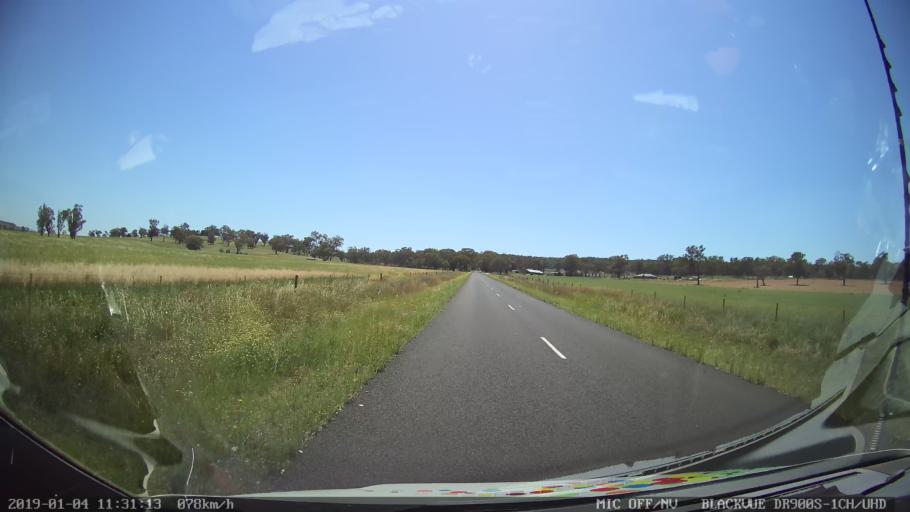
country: AU
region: New South Wales
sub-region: Cabonne
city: Molong
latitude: -33.0733
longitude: 148.7907
